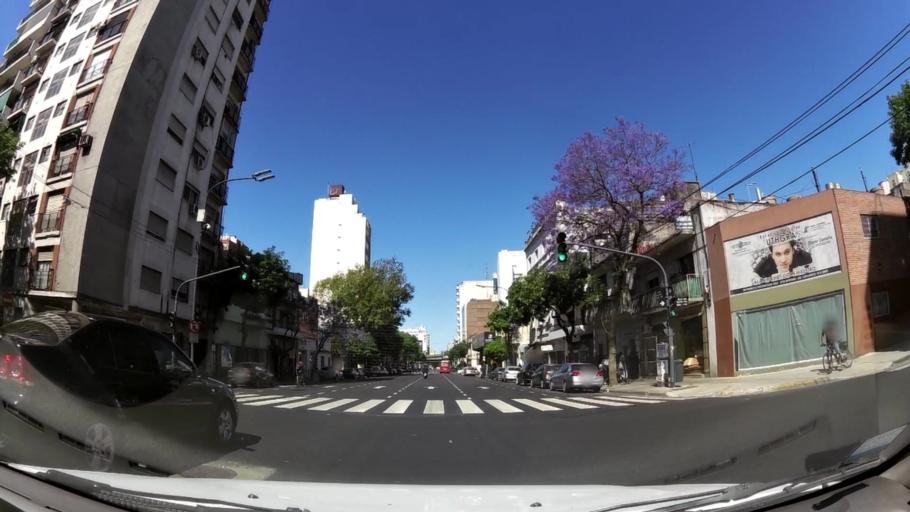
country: AR
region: Buenos Aires F.D.
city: Buenos Aires
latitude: -34.6223
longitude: -58.3844
